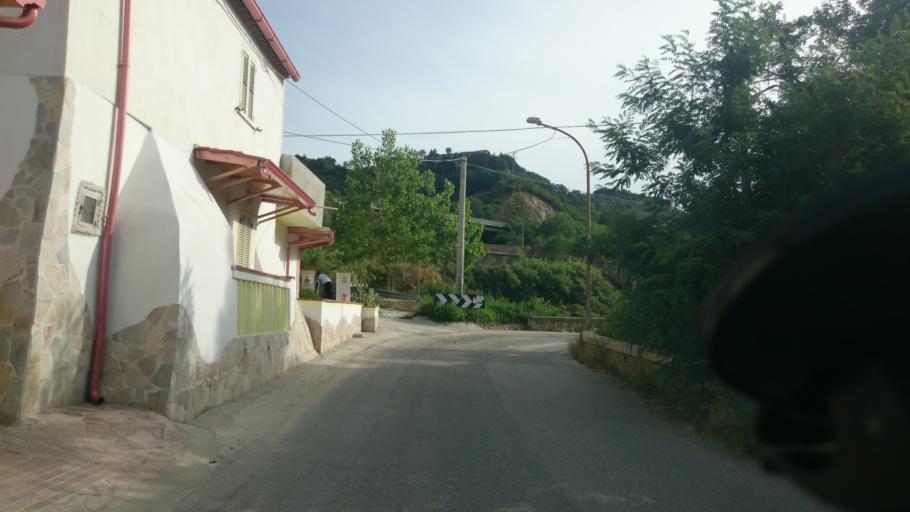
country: IT
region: Calabria
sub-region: Provincia di Vibo-Valentia
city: Drapia
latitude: 38.6748
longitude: 15.9072
